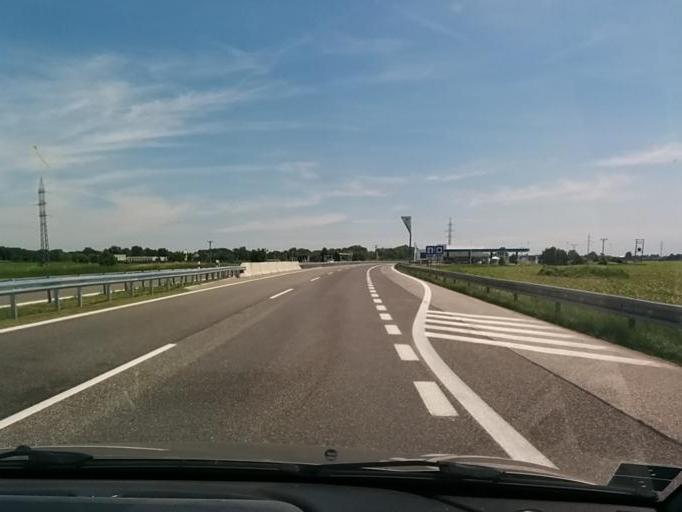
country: SK
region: Trnavsky
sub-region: Okres Galanta
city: Galanta
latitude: 48.2588
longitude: 17.7518
